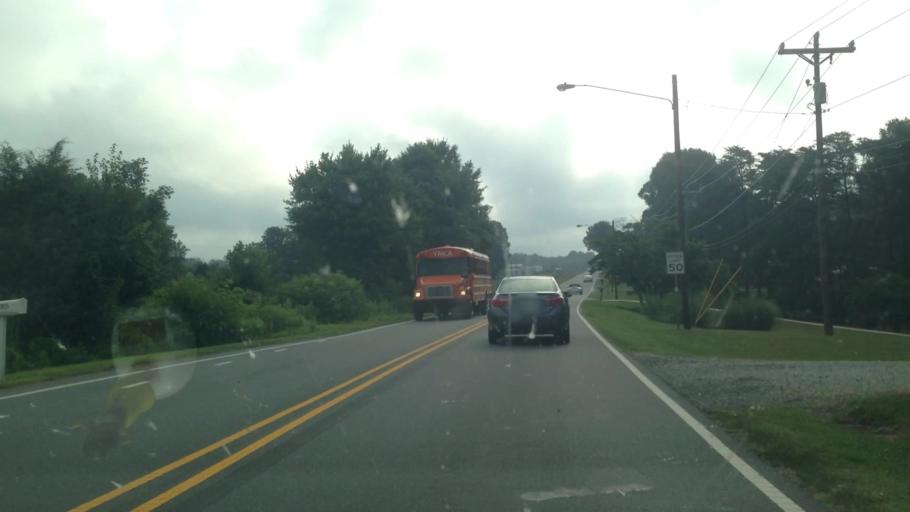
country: US
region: North Carolina
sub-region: Forsyth County
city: Kernersville
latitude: 36.1347
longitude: -80.1165
